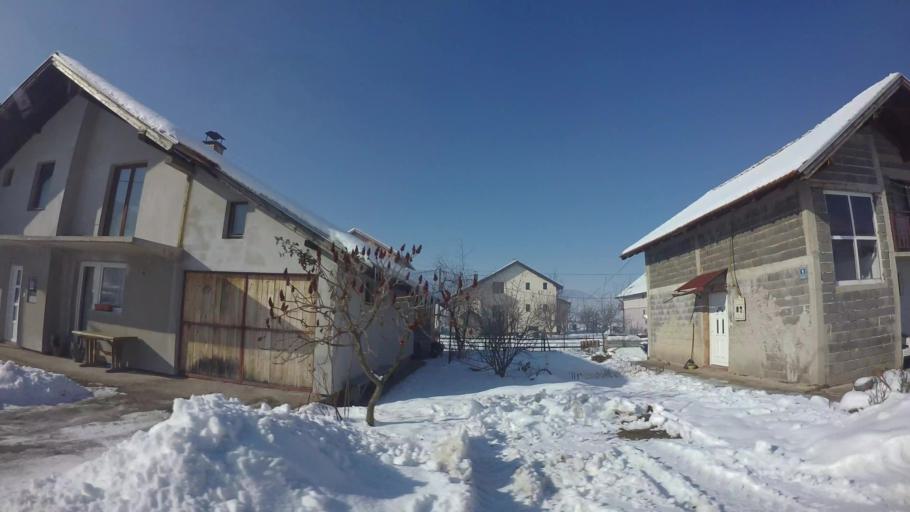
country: BA
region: Federation of Bosnia and Herzegovina
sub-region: Kanton Sarajevo
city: Sarajevo
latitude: 43.7922
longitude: 18.3396
